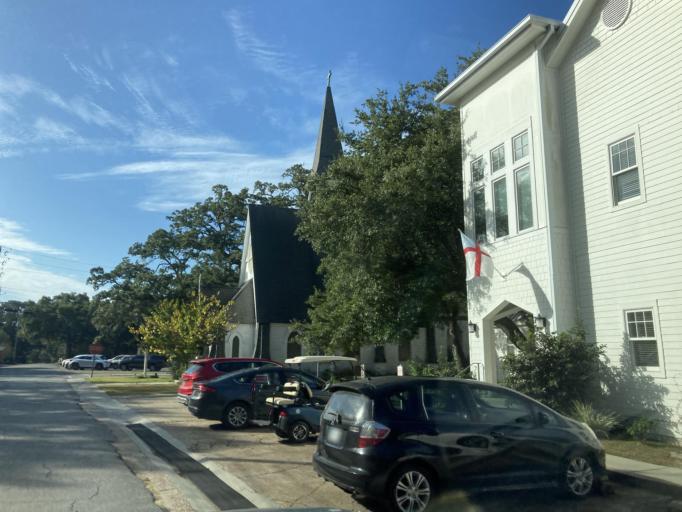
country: US
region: Mississippi
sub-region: Jackson County
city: Ocean Springs
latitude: 30.4125
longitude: -88.8312
